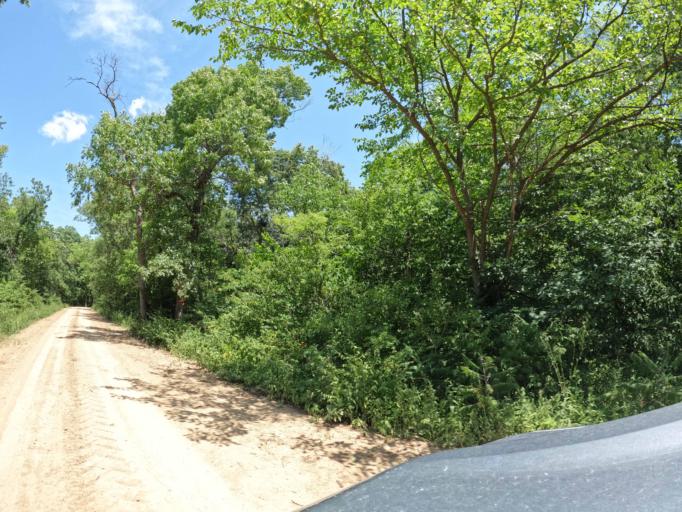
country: US
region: Iowa
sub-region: Henry County
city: Mount Pleasant
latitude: 40.9212
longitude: -91.6652
